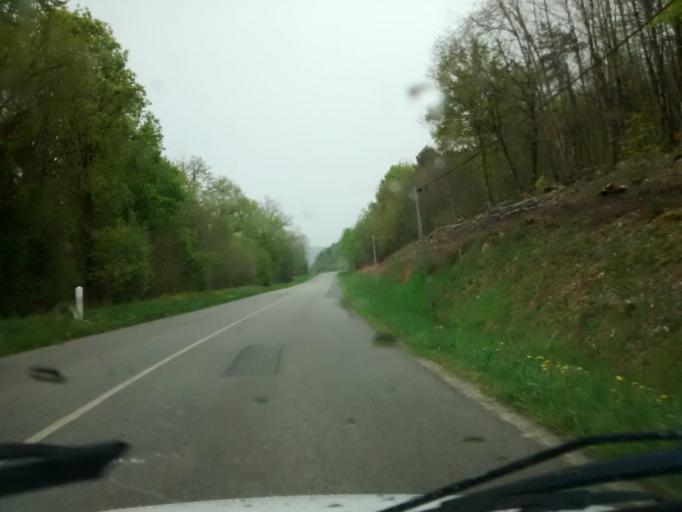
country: FR
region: Brittany
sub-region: Departement du Morbihan
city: Ruffiac
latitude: 47.7895
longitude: -2.3220
